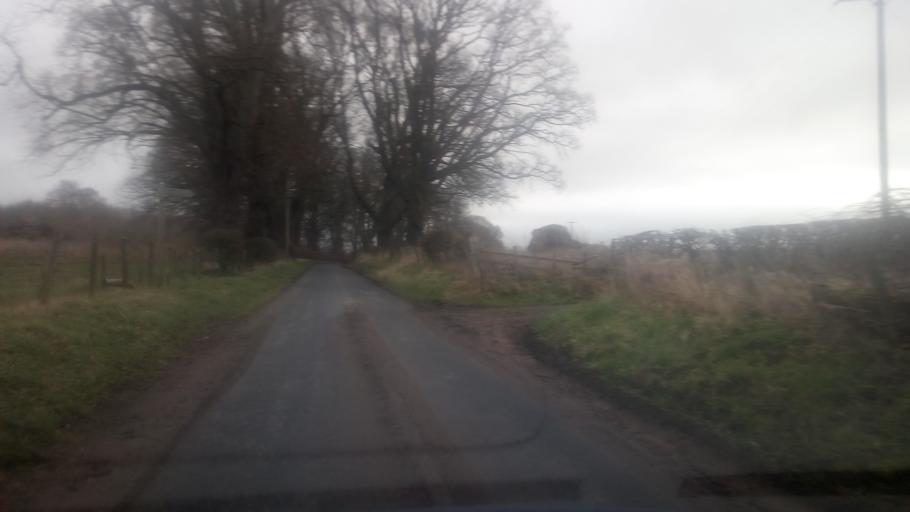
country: GB
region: Scotland
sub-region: The Scottish Borders
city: Jedburgh
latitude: 55.5281
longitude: -2.5138
